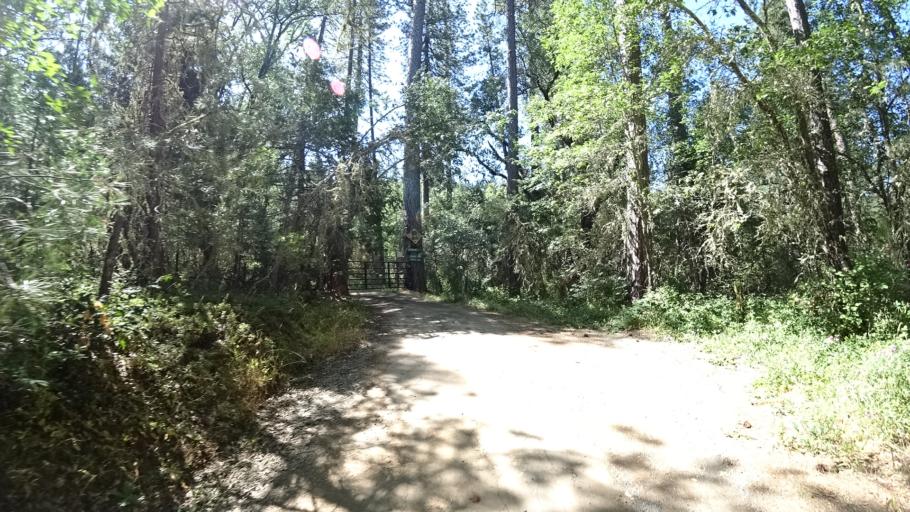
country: US
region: California
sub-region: Amador County
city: Pioneer
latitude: 38.3863
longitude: -120.4954
